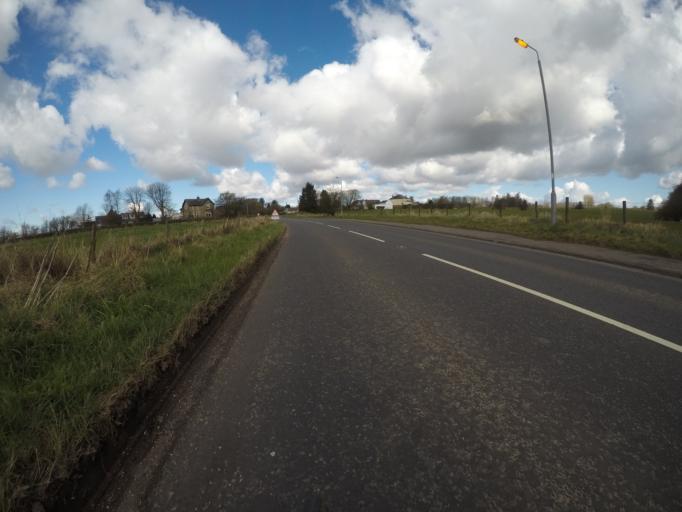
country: GB
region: Scotland
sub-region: North Ayrshire
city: Beith
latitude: 55.7445
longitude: -4.6275
